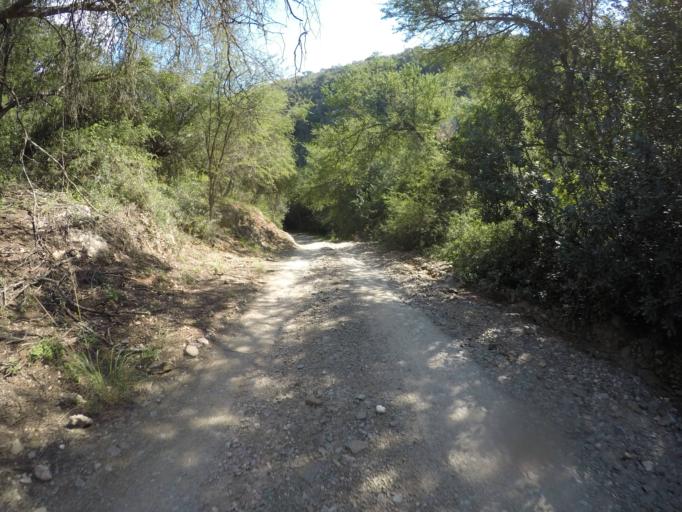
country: ZA
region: Eastern Cape
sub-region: Cacadu District Municipality
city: Kareedouw
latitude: -33.6452
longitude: 24.4523
